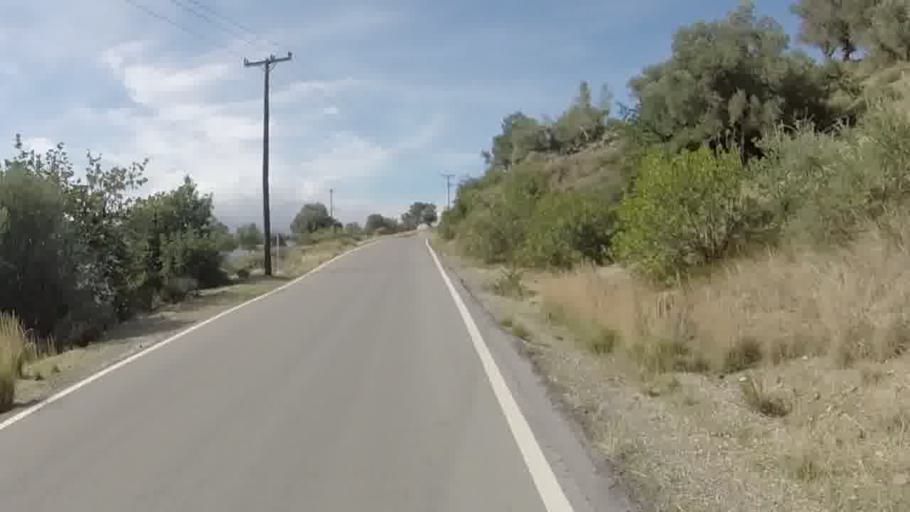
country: GR
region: Crete
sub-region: Nomos Rethymnis
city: Agia Galini
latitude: 35.1460
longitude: 24.7384
